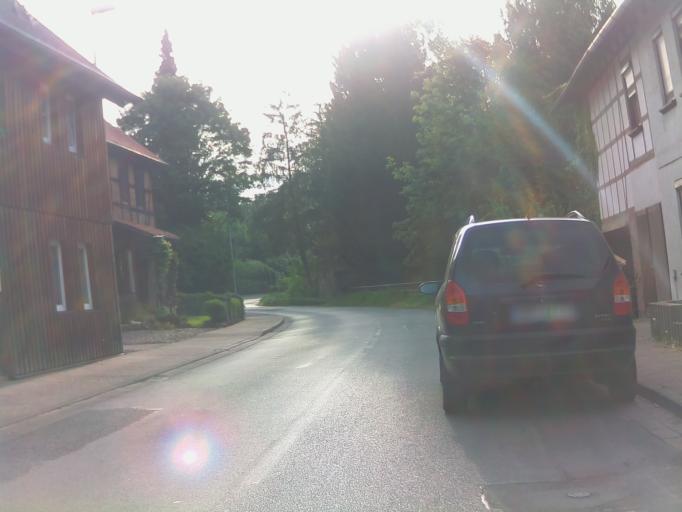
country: DE
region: Lower Saxony
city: Kalefeld
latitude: 51.7936
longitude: 10.0346
